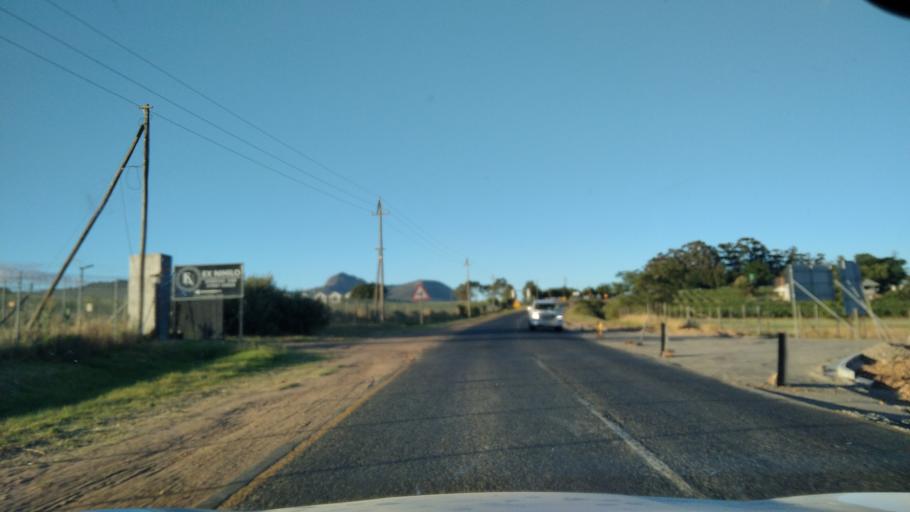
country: ZA
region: Western Cape
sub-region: Cape Winelands District Municipality
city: Paarl
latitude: -33.7972
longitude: 18.9515
